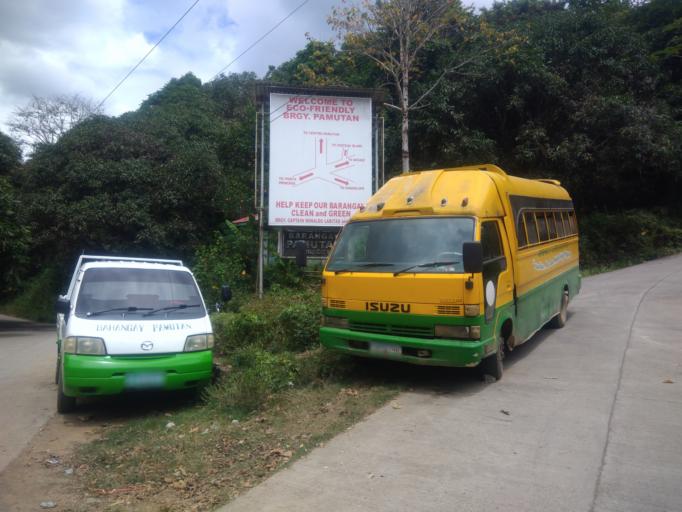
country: PH
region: Western Visayas
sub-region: Province of Negros Occidental
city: Jaclupan
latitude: 10.3367
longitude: 123.8425
